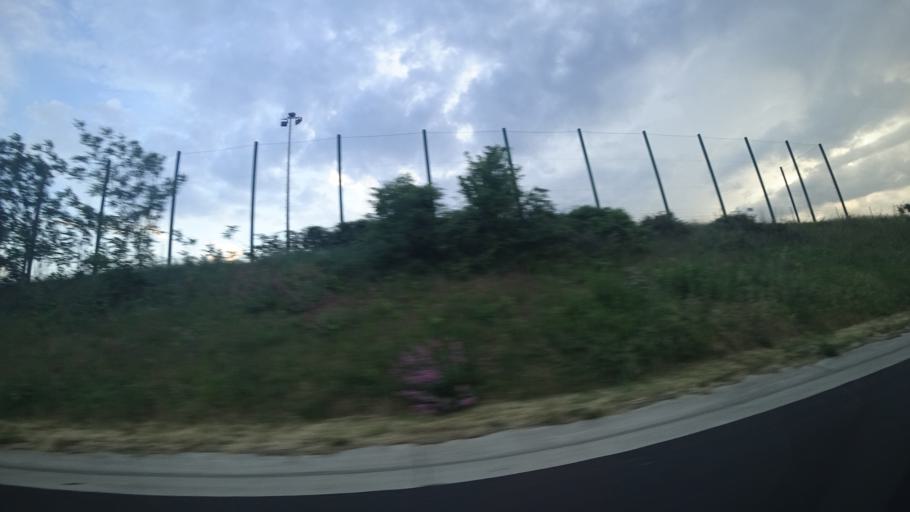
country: FR
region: Languedoc-Roussillon
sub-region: Departement de l'Herault
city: Nebian
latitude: 43.6371
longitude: 3.4467
